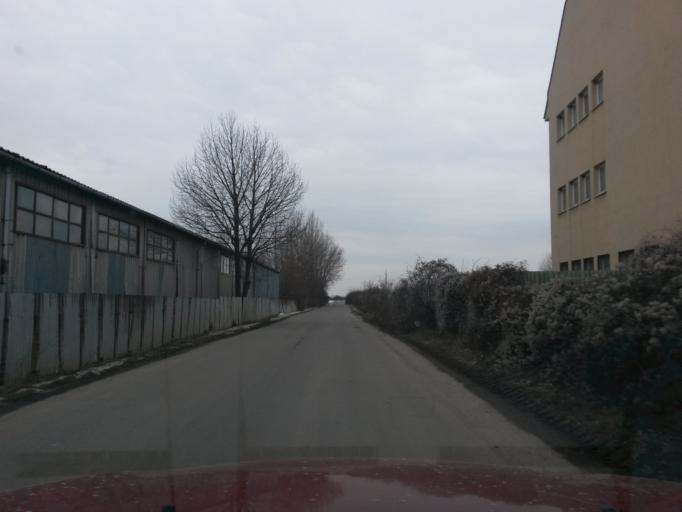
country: SK
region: Kosicky
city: Michalovce
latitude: 48.7461
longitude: 21.8896
